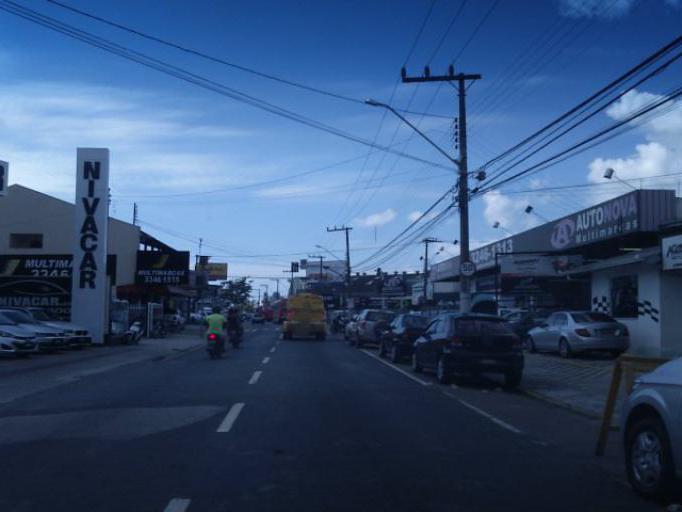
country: BR
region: Santa Catarina
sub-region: Itajai
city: Itajai
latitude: -26.8932
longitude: -48.6783
